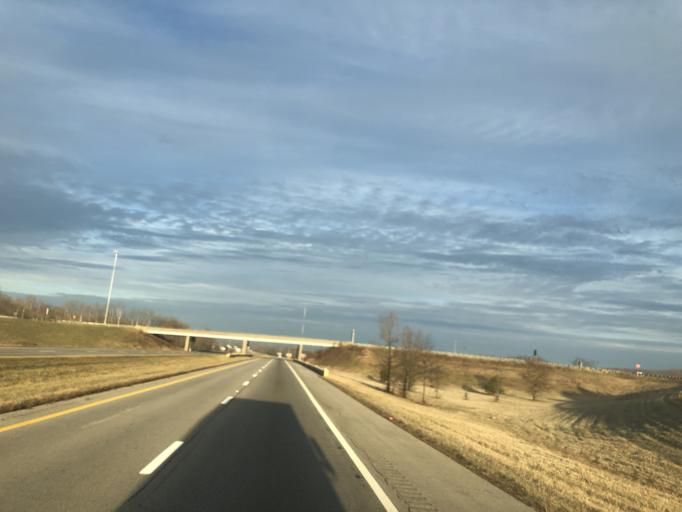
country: US
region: Ohio
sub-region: Hocking County
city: Logan
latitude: 39.5208
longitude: -82.3743
